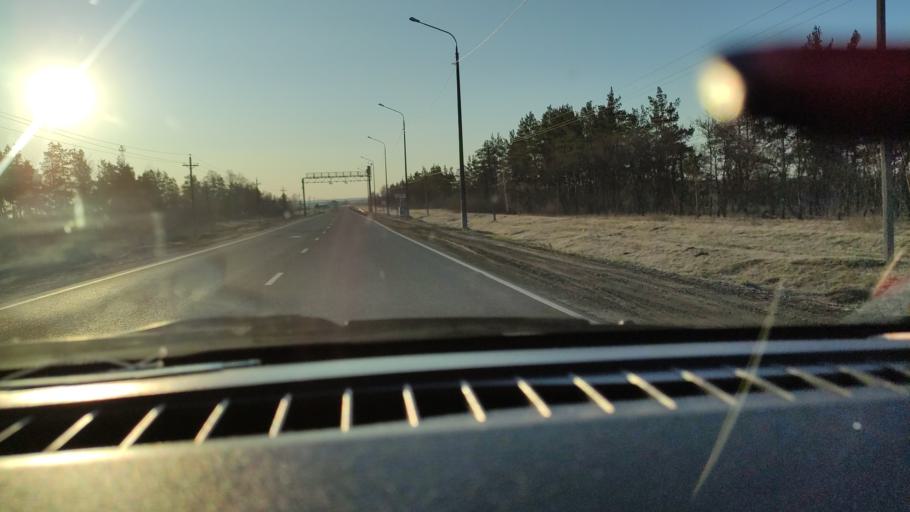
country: RU
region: Saratov
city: Sennoy
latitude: 52.1517
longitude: 46.9687
